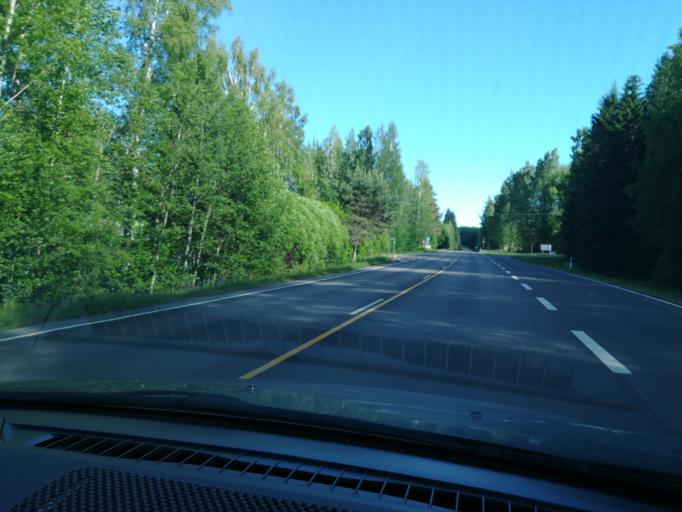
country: FI
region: Southern Savonia
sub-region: Mikkeli
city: Puumala
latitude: 61.5117
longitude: 28.1796
